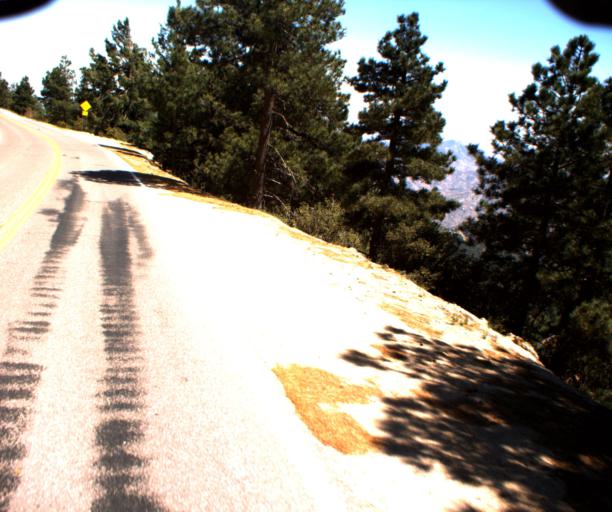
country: US
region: Arizona
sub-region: Graham County
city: Swift Trail Junction
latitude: 32.6212
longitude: -109.8276
